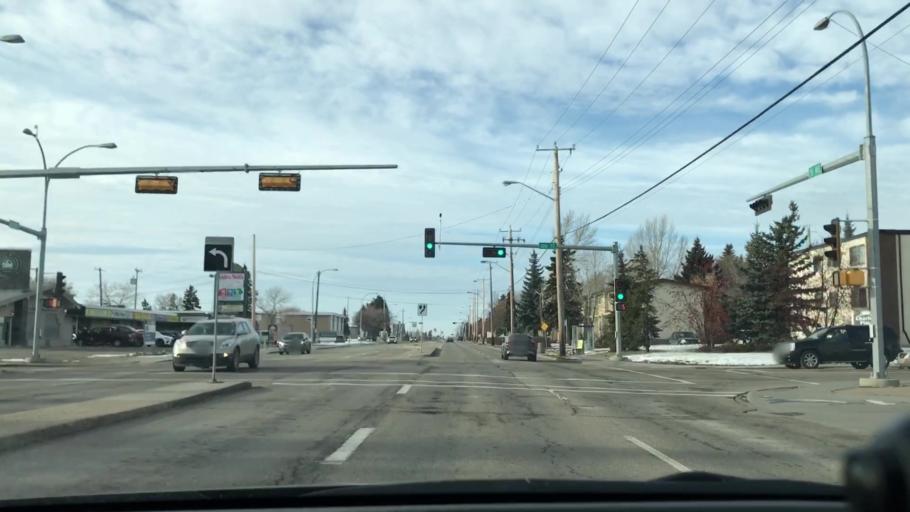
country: CA
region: Alberta
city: Edmonton
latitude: 53.4883
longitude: -113.5040
